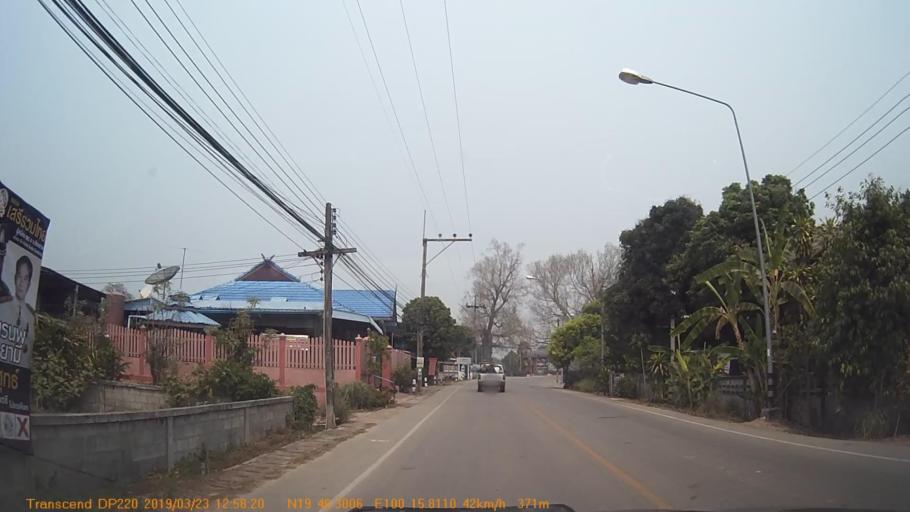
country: TH
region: Chiang Rai
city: Thoeng
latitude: 19.6718
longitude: 100.2636
